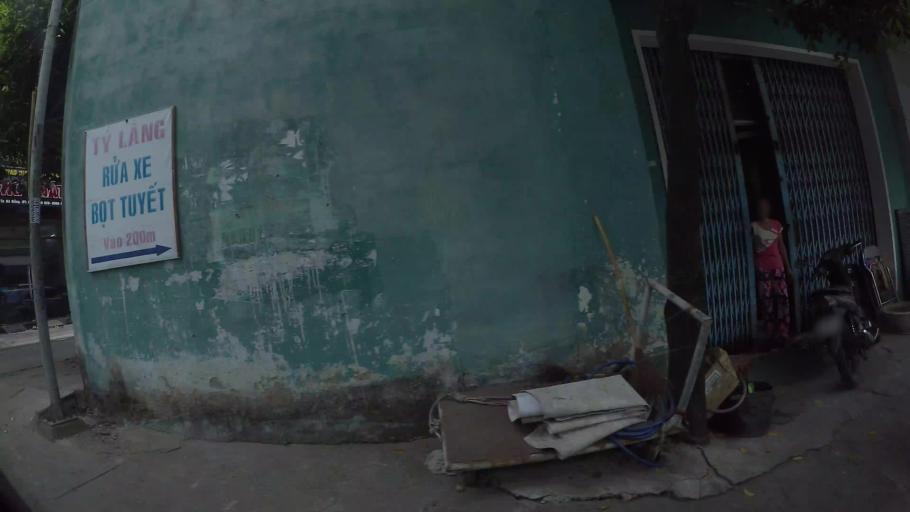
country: VN
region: Da Nang
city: Thanh Khe
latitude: 16.0651
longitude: 108.1890
